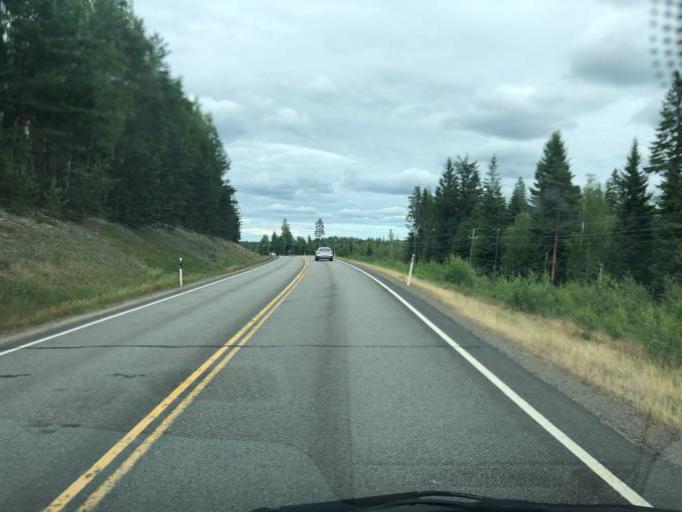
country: FI
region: Kymenlaakso
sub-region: Kouvola
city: Kouvola
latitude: 60.9732
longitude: 26.9011
